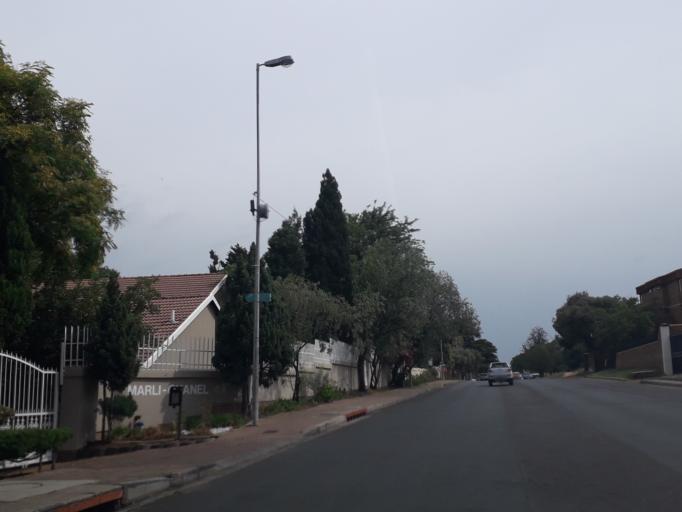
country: ZA
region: Gauteng
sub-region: City of Johannesburg Metropolitan Municipality
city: Johannesburg
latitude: -26.0984
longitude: 27.9956
